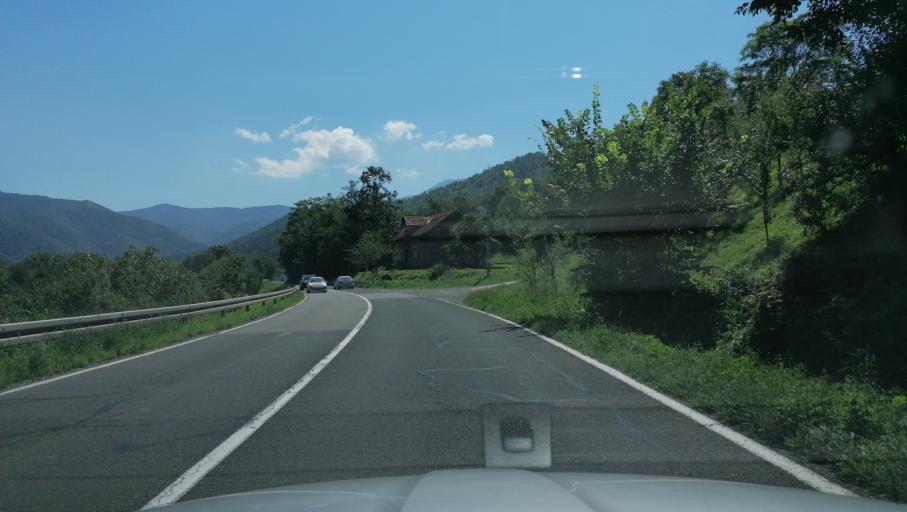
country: RS
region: Central Serbia
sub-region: Raski Okrug
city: Kraljevo
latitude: 43.6754
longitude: 20.5726
